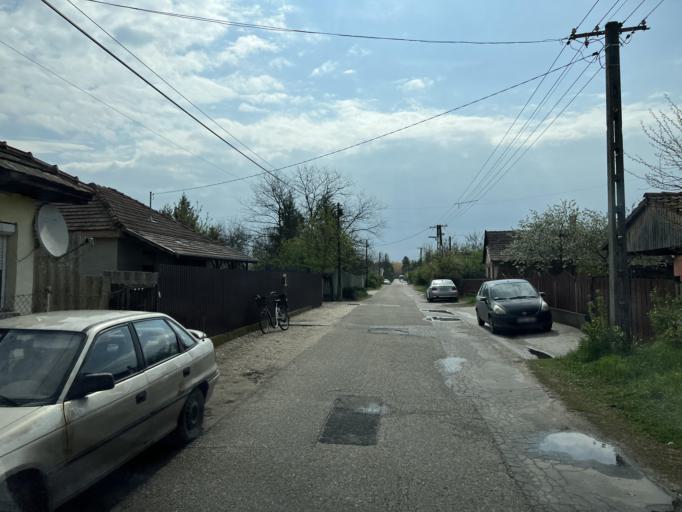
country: HU
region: Pest
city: Hernad
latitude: 47.1772
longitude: 19.4684
